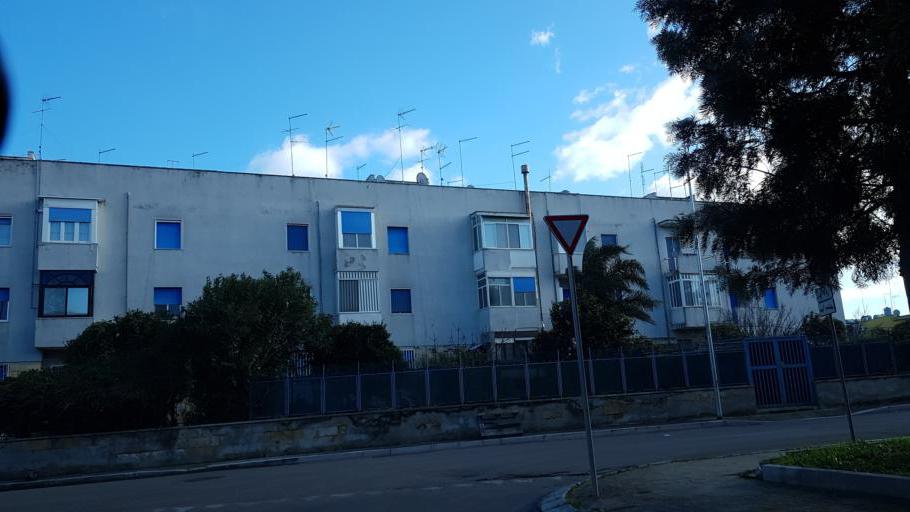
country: IT
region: Apulia
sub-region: Provincia di Brindisi
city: Brindisi
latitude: 40.6490
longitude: 17.9177
